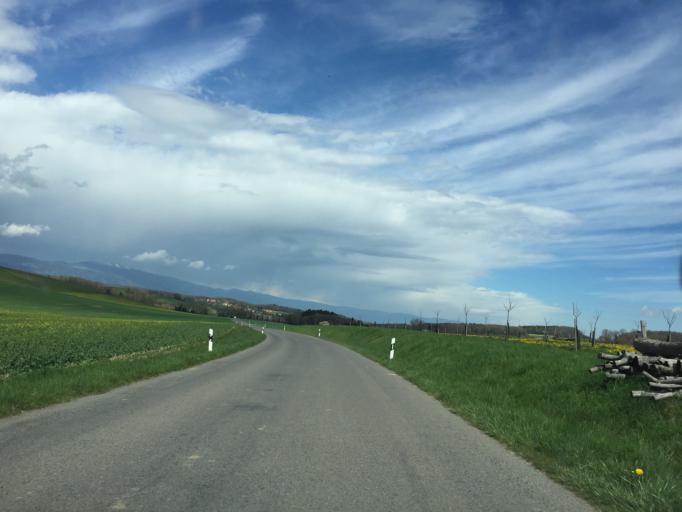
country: CH
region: Vaud
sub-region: Morges District
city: La Chaux
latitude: 46.6208
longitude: 6.4719
